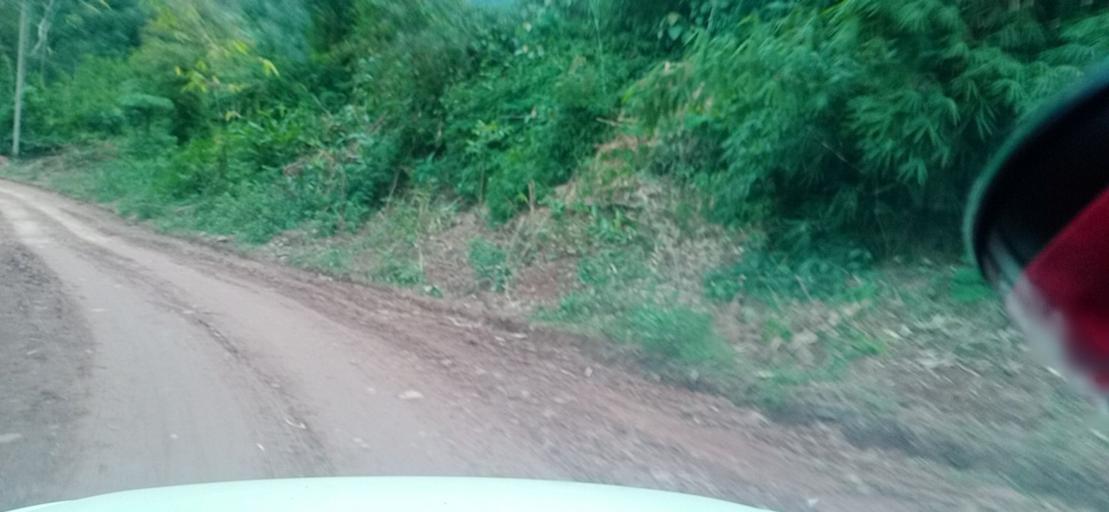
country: TH
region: Changwat Bueng Kan
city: Pak Khat
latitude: 18.5517
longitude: 103.4283
